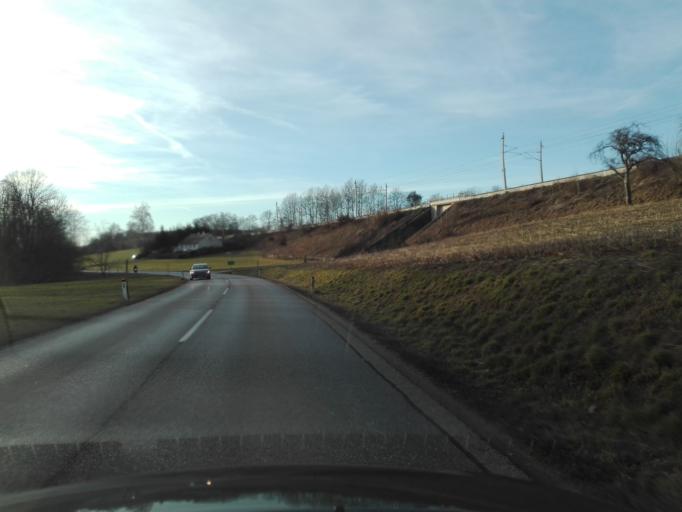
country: AT
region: Lower Austria
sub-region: Politischer Bezirk Amstetten
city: Haag
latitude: 48.1165
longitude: 14.5478
